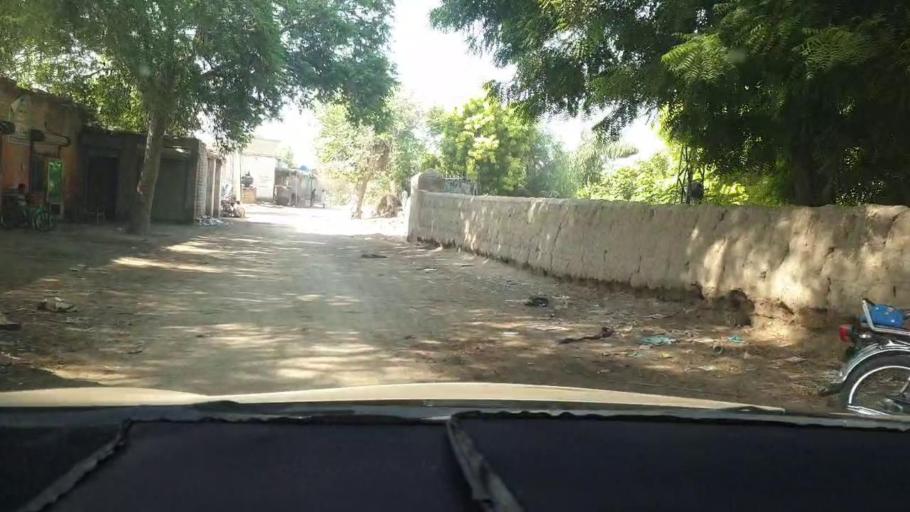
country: PK
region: Sindh
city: Kambar
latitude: 27.6067
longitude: 68.0929
